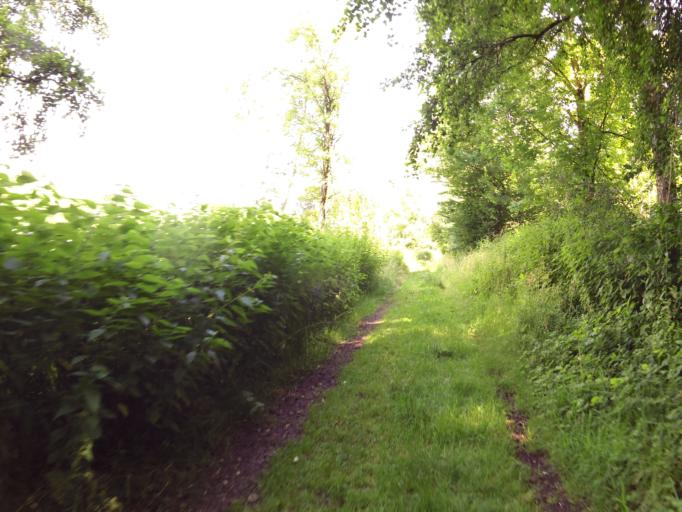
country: DE
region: Baden-Wuerttemberg
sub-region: Freiburg Region
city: Lahr
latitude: 48.3264
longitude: 7.8614
